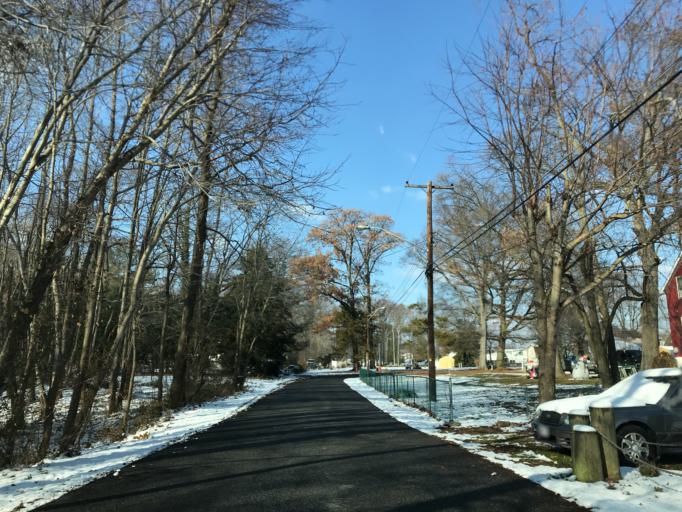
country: US
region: Maryland
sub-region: Baltimore County
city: Bowleys Quarters
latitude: 39.3161
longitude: -76.3779
